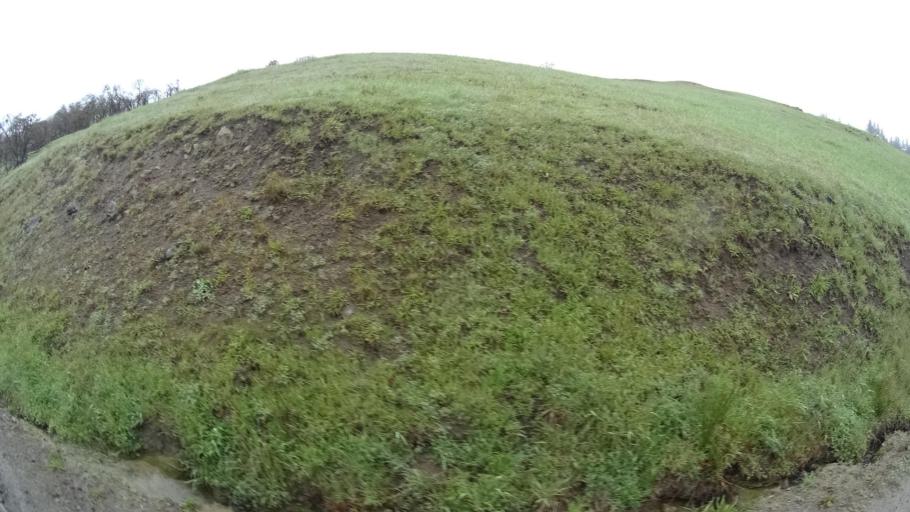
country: US
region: California
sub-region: Humboldt County
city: Westhaven-Moonstone
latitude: 41.1471
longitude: -123.8789
